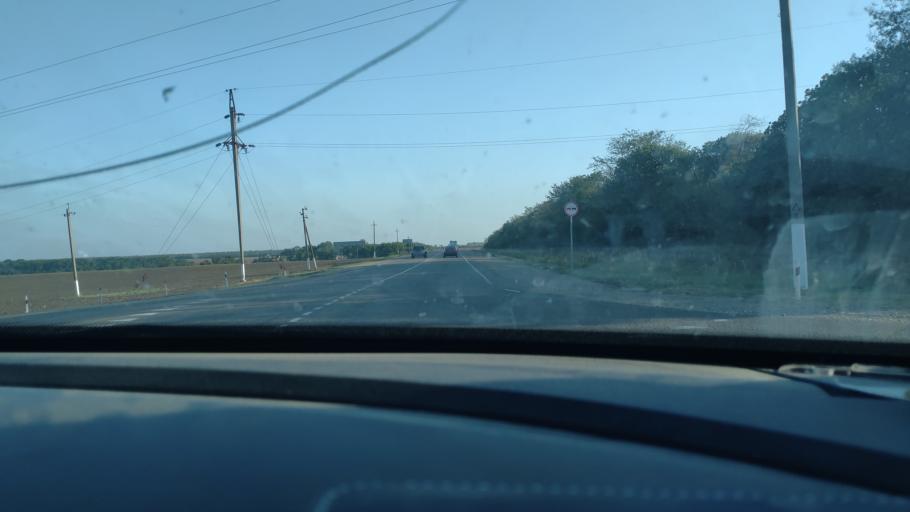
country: RU
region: Krasnodarskiy
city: Novominskaya
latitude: 46.2986
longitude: 38.9330
